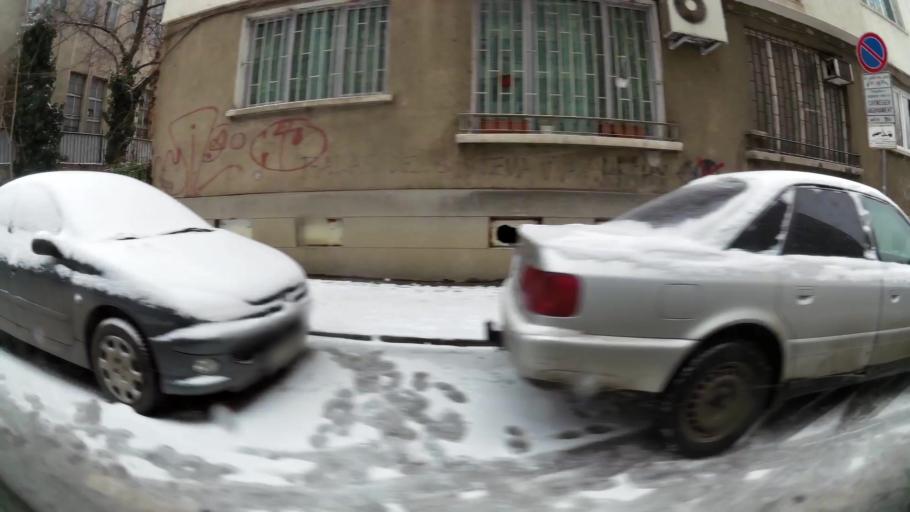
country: BG
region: Sofia-Capital
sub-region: Stolichna Obshtina
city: Sofia
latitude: 42.6979
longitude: 23.3363
